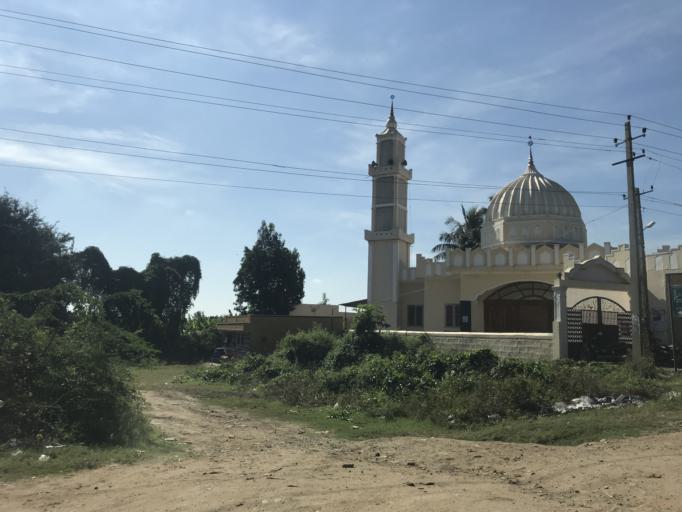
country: IN
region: Karnataka
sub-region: Mysore
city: Heggadadevankote
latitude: 12.0653
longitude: 76.3538
